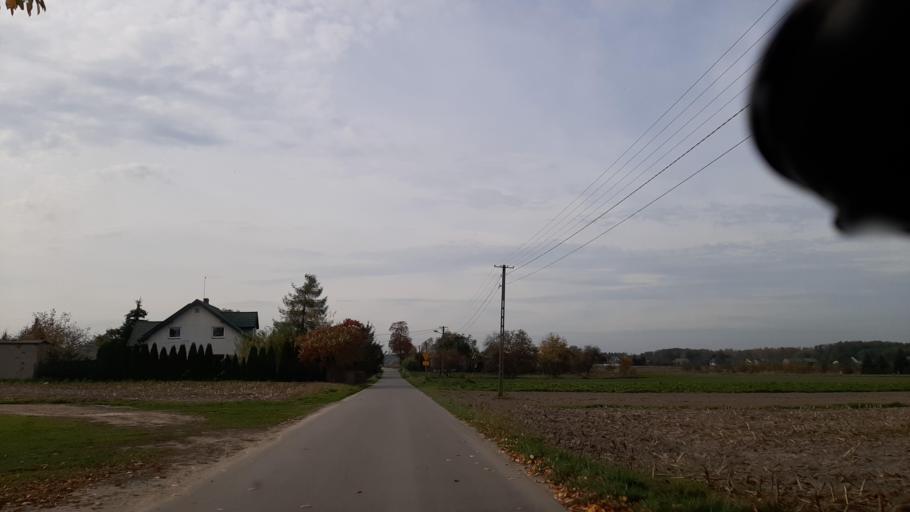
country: PL
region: Lublin Voivodeship
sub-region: Powiat lubelski
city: Garbow
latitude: 51.3920
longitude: 22.3181
